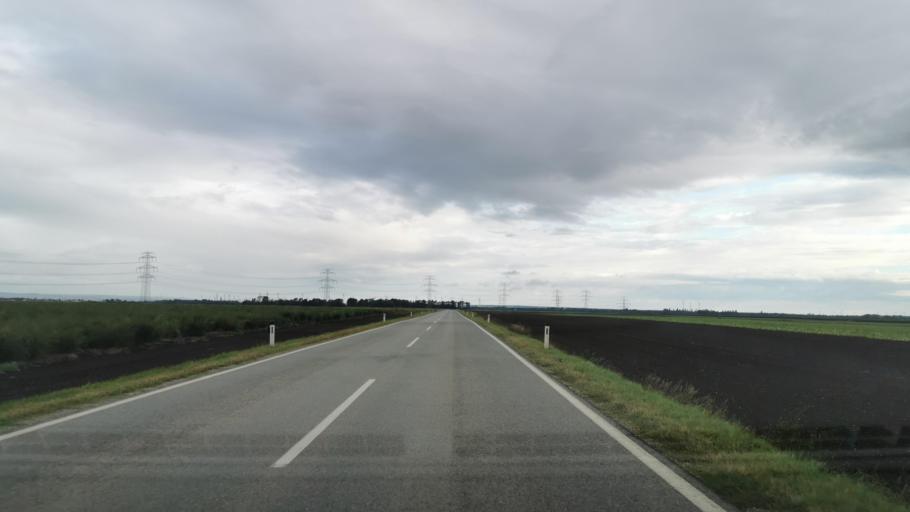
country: AT
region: Lower Austria
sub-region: Politischer Bezirk Ganserndorf
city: Raasdorf
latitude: 48.2539
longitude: 16.5614
